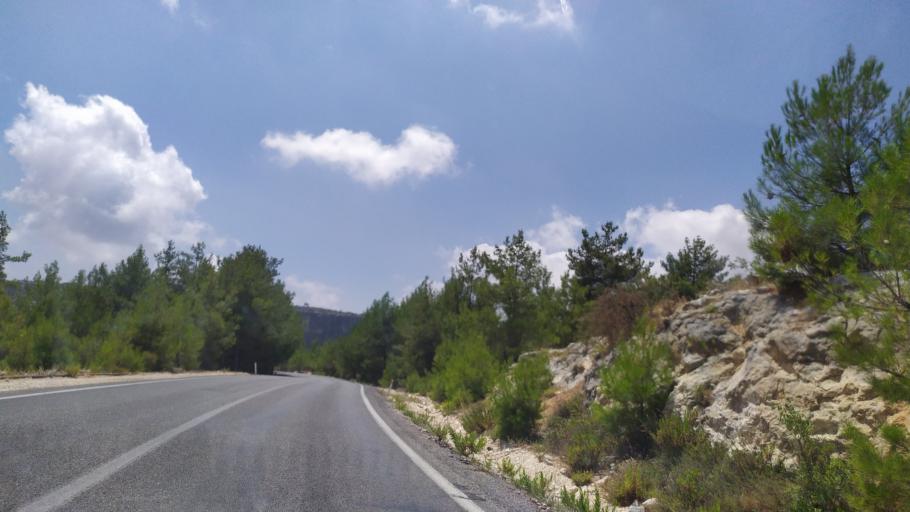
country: TR
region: Mersin
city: Gulnar
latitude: 36.2778
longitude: 33.3885
